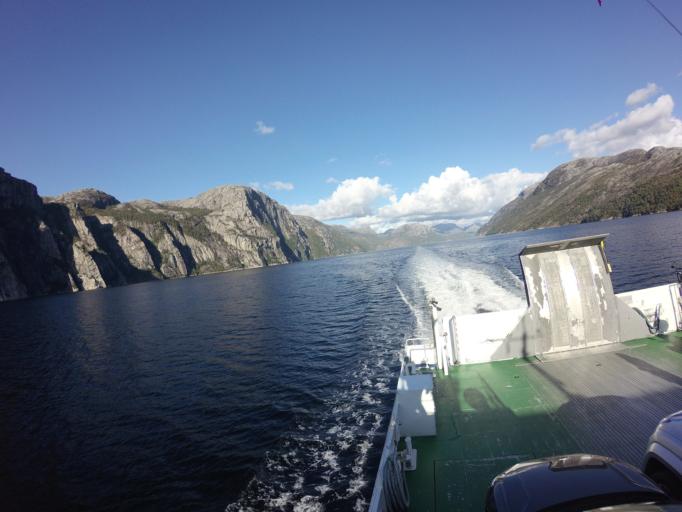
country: NO
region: Rogaland
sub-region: Forsand
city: Forsand
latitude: 58.9800
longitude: 6.2047
